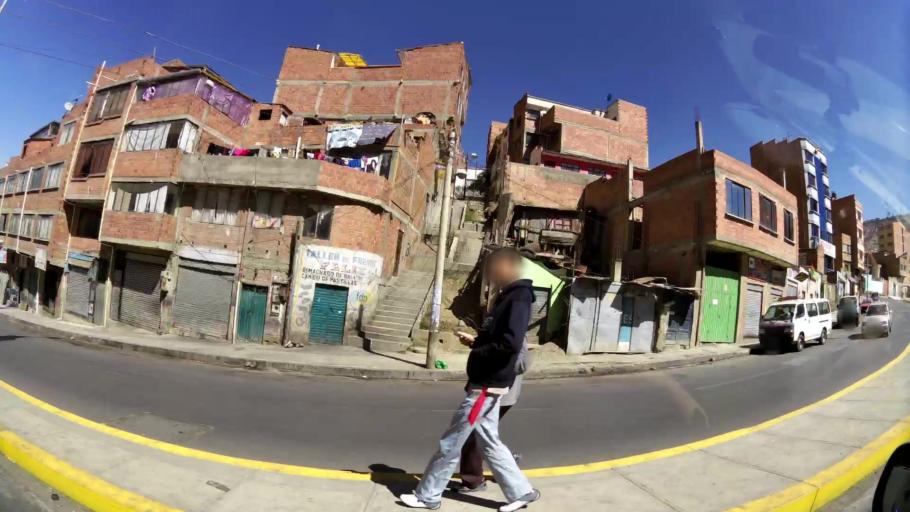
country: BO
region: La Paz
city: La Paz
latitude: -16.4931
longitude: -68.1500
